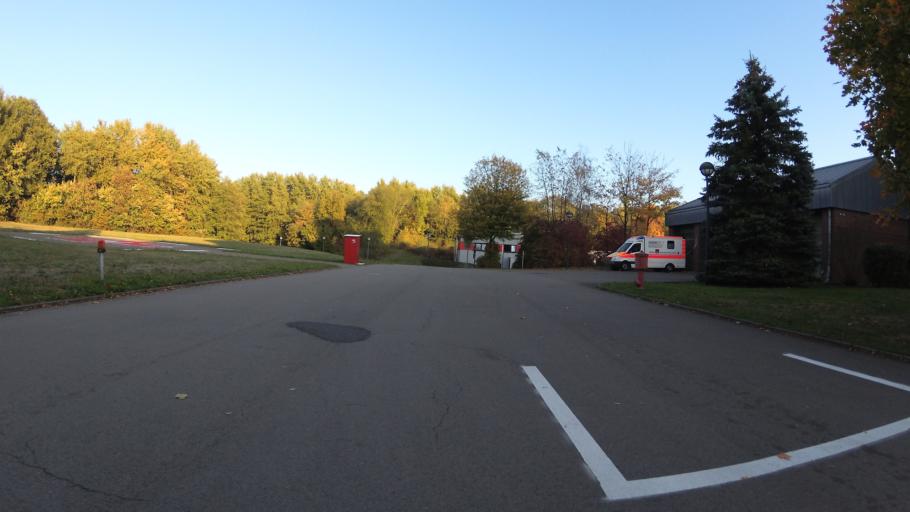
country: DE
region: Saarland
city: Sankt Wendel
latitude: 49.4544
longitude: 7.1793
